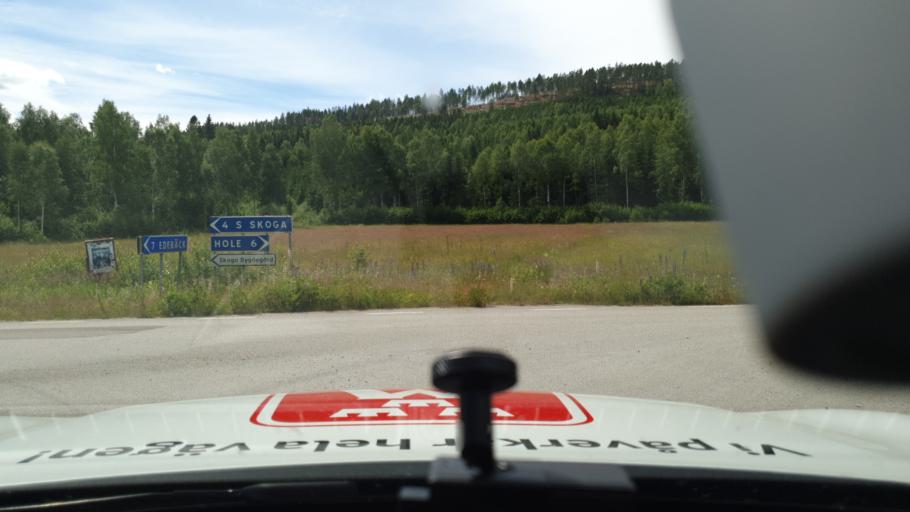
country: SE
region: Vaermland
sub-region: Hagfors Kommun
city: Ekshaerad
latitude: 60.0678
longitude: 13.4776
